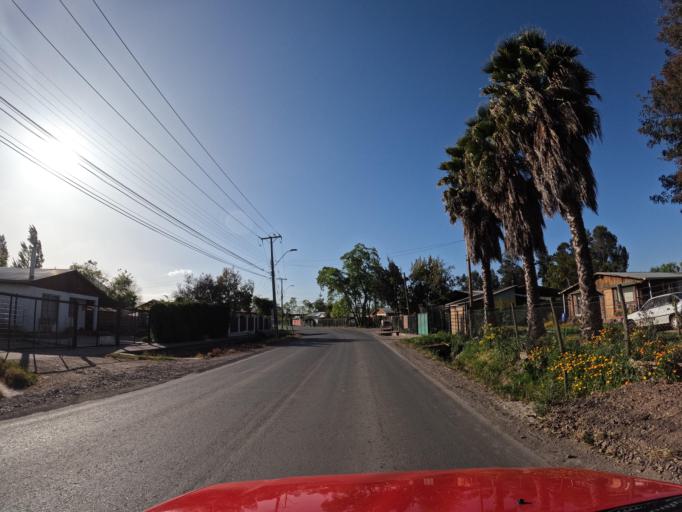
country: CL
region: O'Higgins
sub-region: Provincia de Colchagua
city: Santa Cruz
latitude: -34.7117
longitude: -71.2909
